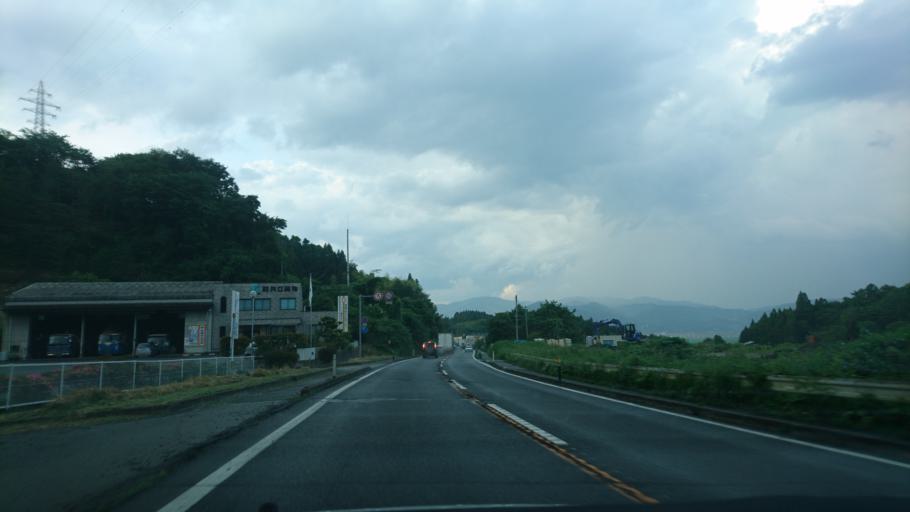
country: JP
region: Iwate
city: Ichinoseki
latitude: 38.9491
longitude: 141.1188
